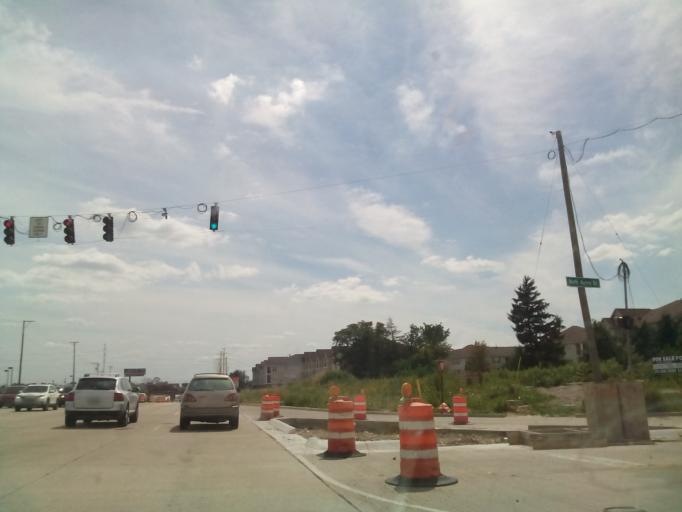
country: US
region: Illinois
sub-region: DuPage County
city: Warrenville
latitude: 41.7812
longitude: -88.2059
